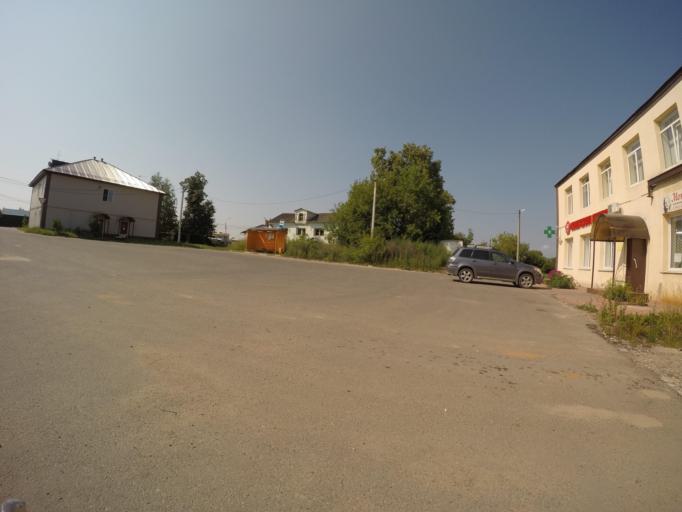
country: RU
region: Moskovskaya
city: Rechitsy
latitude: 55.6144
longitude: 38.5359
